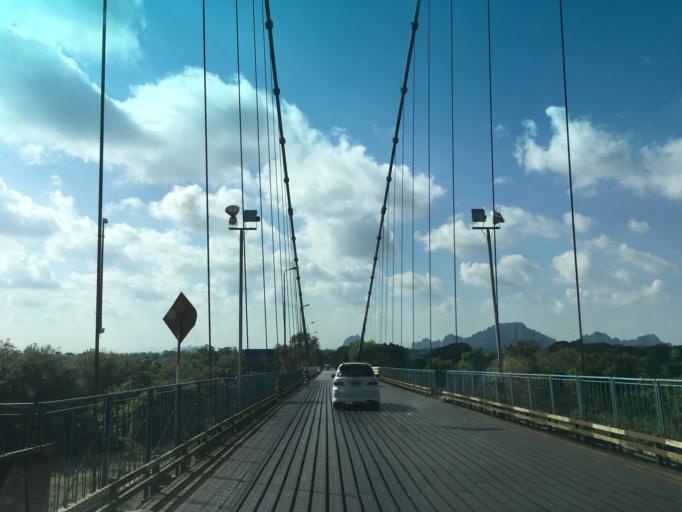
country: MM
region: Mon
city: Martaban
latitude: 16.5619
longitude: 97.7320
